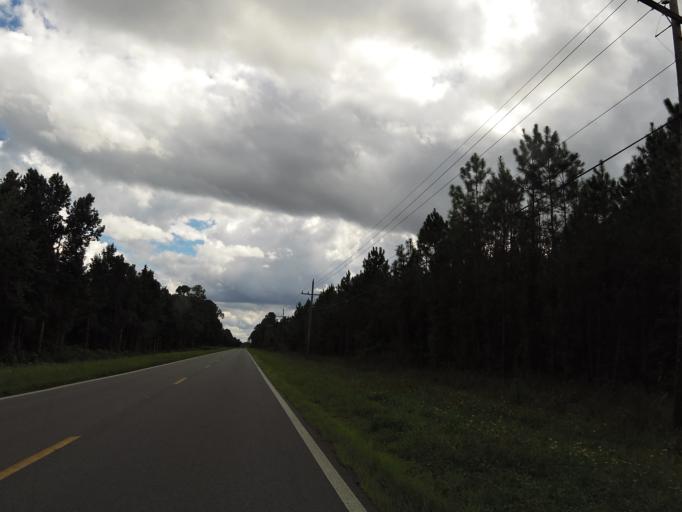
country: US
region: Florida
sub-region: Saint Johns County
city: Saint Augustine South
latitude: 29.8659
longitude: -81.4942
